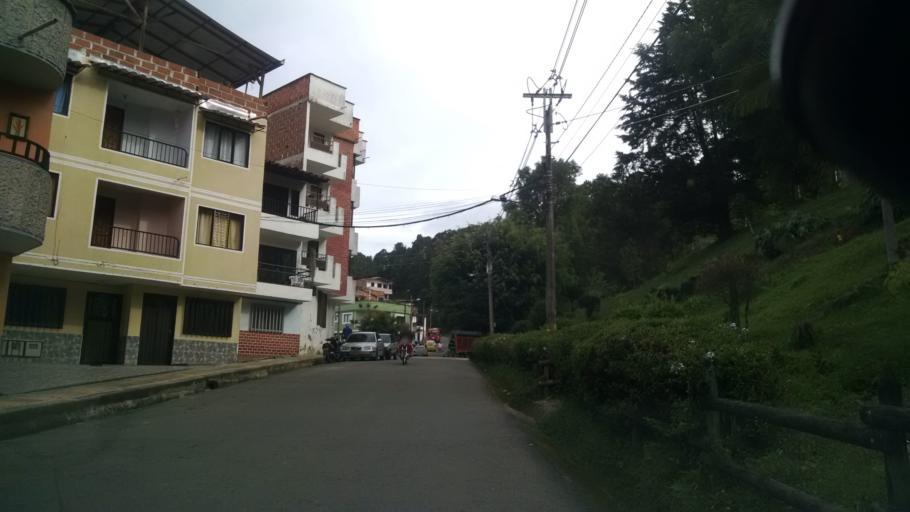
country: CO
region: Antioquia
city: Santuario
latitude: 6.2175
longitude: -75.2459
